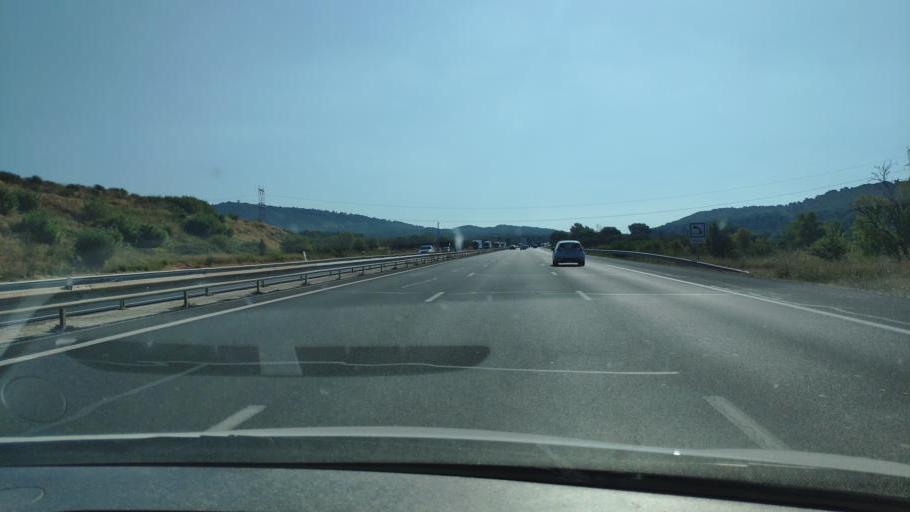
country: FR
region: Provence-Alpes-Cote d'Azur
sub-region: Departement des Bouches-du-Rhone
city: Coudoux
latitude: 43.5531
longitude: 5.2584
